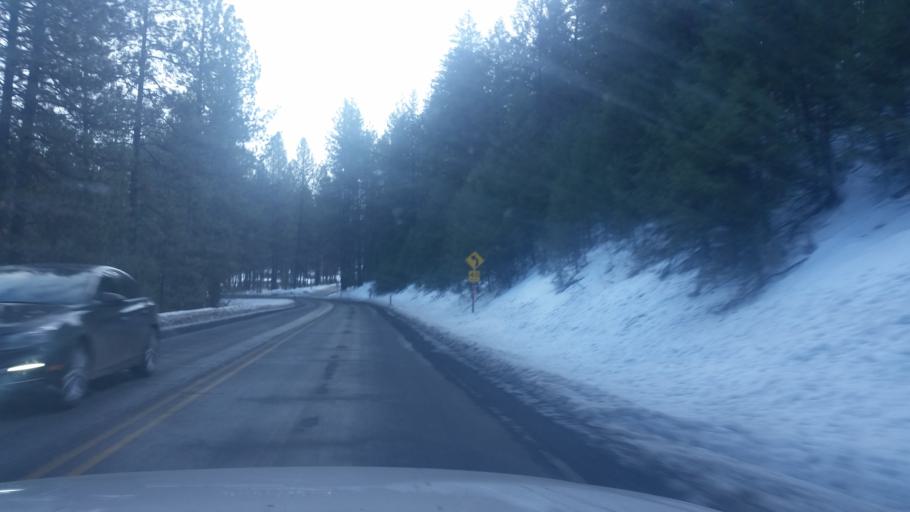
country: US
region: Washington
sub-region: Spokane County
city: Fairchild Air Force Base
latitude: 47.8371
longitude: -117.8566
